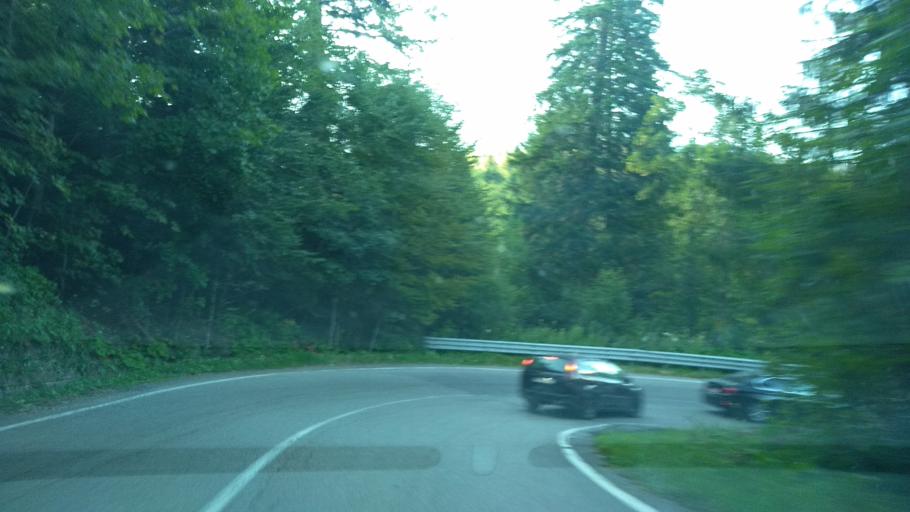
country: RO
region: Prahova
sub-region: Oras Sinaia
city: Sinaia
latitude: 45.3278
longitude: 25.5207
